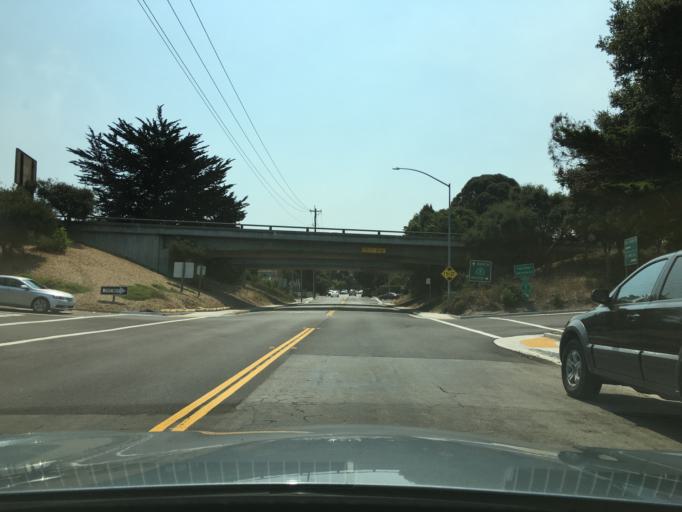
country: US
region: California
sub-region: Monterey County
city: Seaside
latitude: 36.5994
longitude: -121.8651
